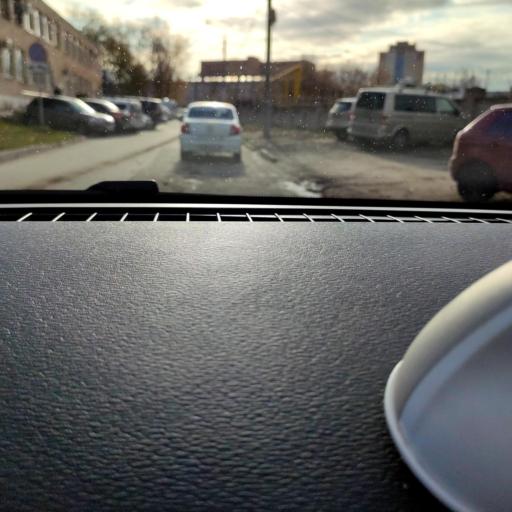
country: RU
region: Samara
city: Samara
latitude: 53.2023
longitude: 50.1663
